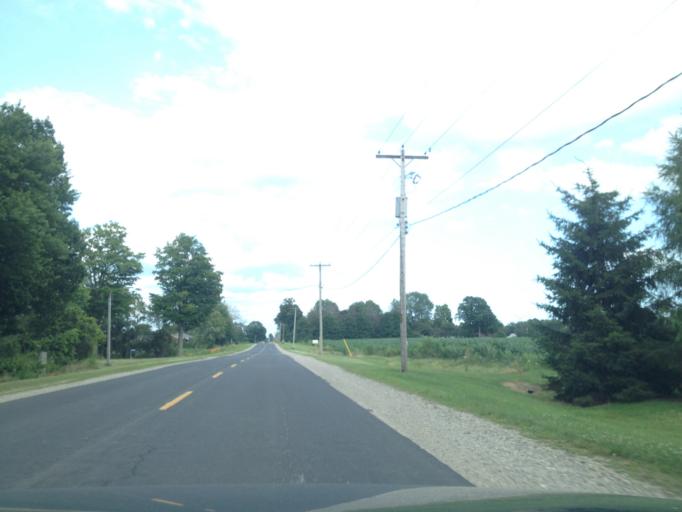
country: CA
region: Ontario
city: Aylmer
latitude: 42.6748
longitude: -80.9319
